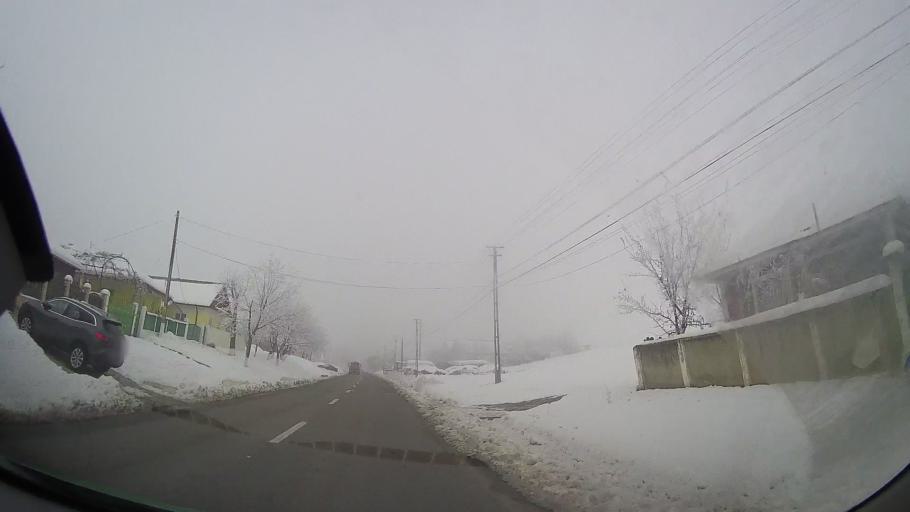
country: RO
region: Iasi
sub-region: Comuna Halaucesti
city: Halaucesti
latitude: 47.0981
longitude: 26.8183
